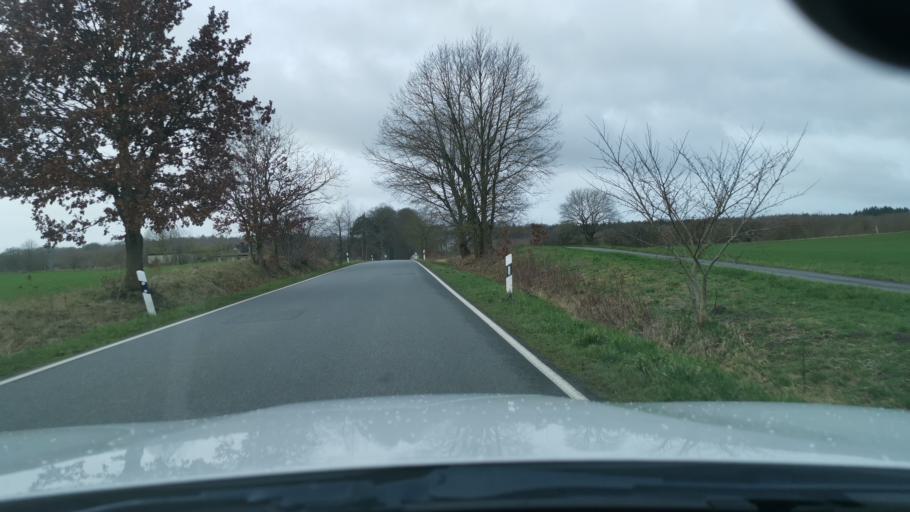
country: DE
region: Mecklenburg-Vorpommern
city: Wardow
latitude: 54.0042
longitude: 12.3935
